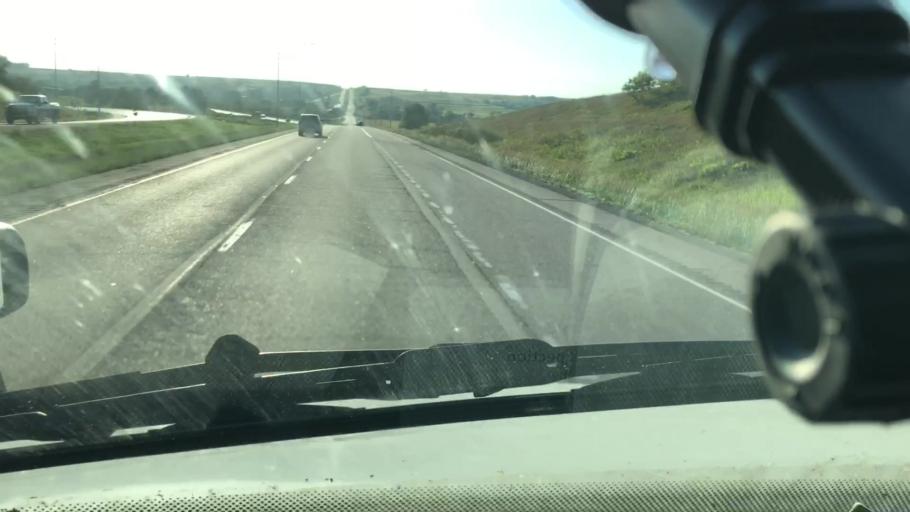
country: US
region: Iowa
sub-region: Pottawattamie County
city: Avoca
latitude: 41.4990
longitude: -95.5752
